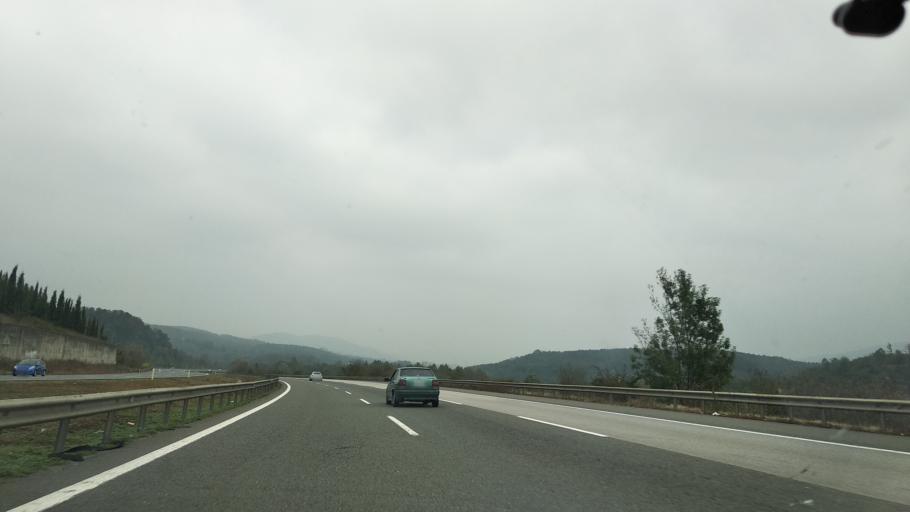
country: TR
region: Sakarya
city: Hendek
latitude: 40.7719
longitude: 30.7822
